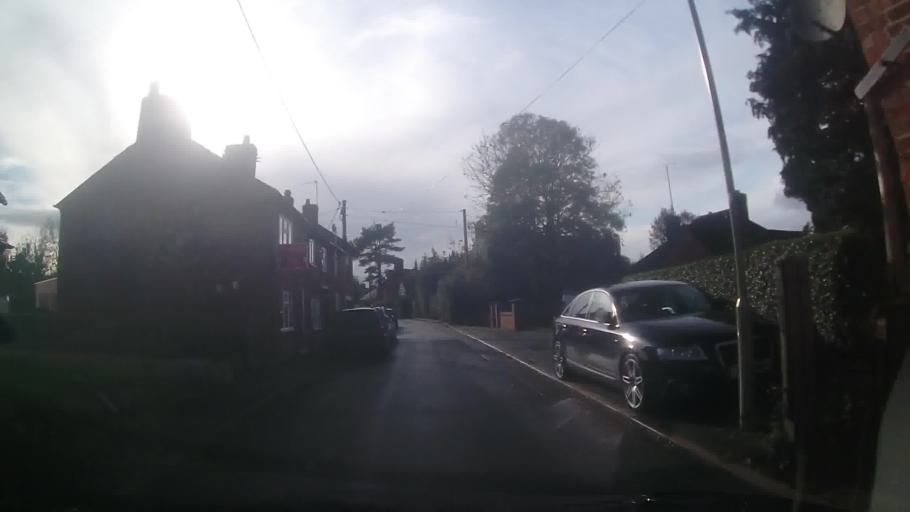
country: GB
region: England
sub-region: Shropshire
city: Whitchurch
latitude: 52.9651
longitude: -2.6854
